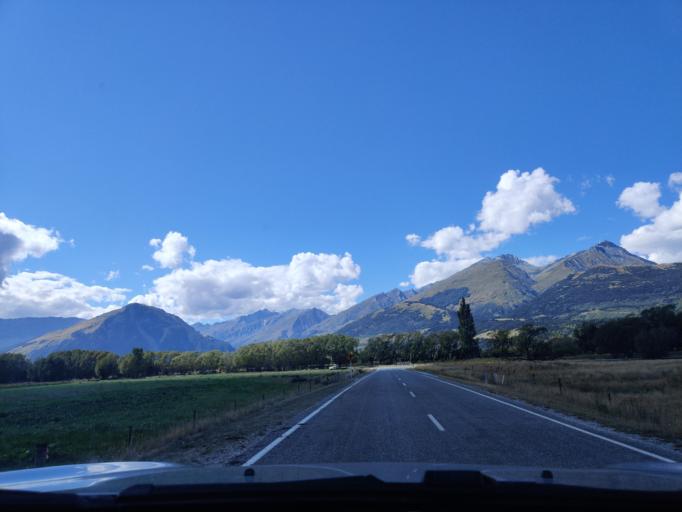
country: NZ
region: Otago
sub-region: Queenstown-Lakes District
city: Queenstown
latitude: -44.7838
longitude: 168.3928
